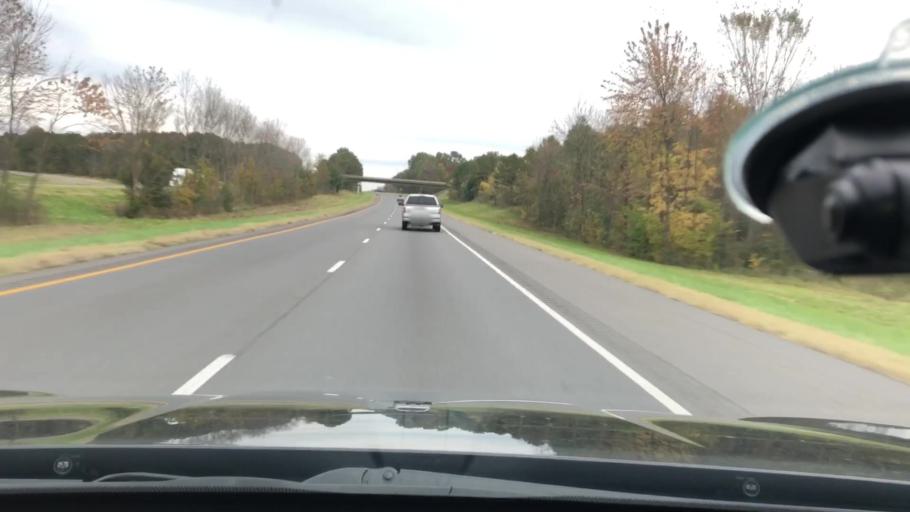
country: US
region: Arkansas
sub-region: Hempstead County
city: Hope
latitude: 33.7355
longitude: -93.5259
